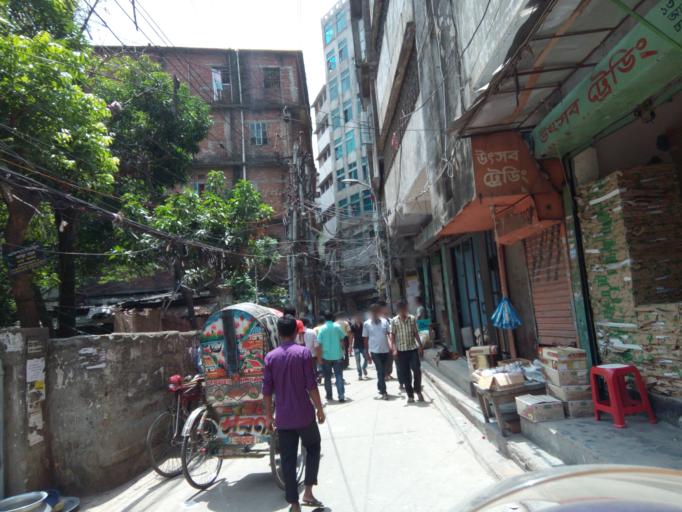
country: BD
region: Dhaka
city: Paltan
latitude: 23.7325
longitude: 90.4176
